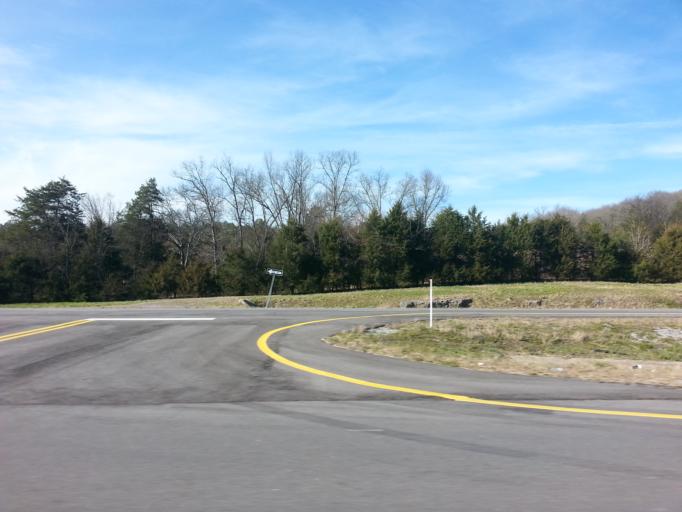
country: US
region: Tennessee
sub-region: Cannon County
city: Woodbury
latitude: 35.8054
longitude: -86.1357
